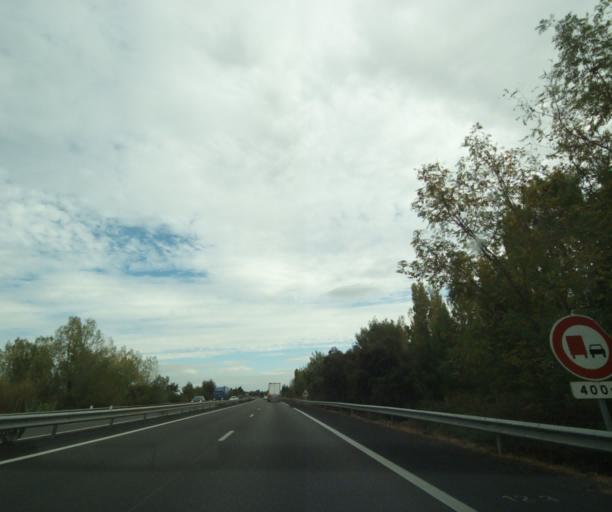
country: FR
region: Languedoc-Roussillon
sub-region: Departement du Gard
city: Garons
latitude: 43.7421
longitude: 4.4477
